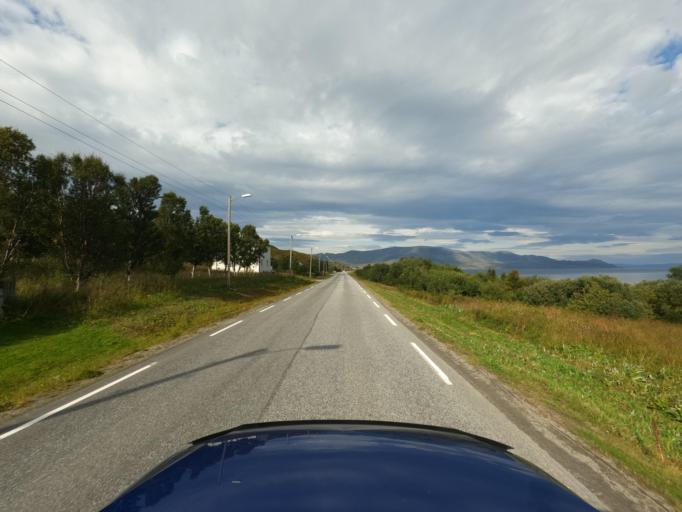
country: NO
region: Finnmark Fylke
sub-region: Kvalsund
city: Kvalsund
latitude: 70.5069
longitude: 24.0530
